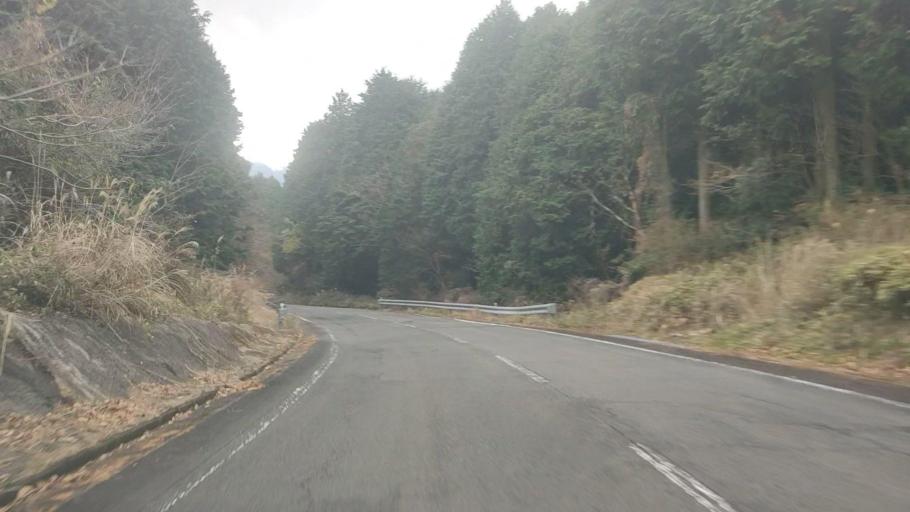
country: JP
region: Nagasaki
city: Shimabara
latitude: 32.7925
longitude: 130.2813
